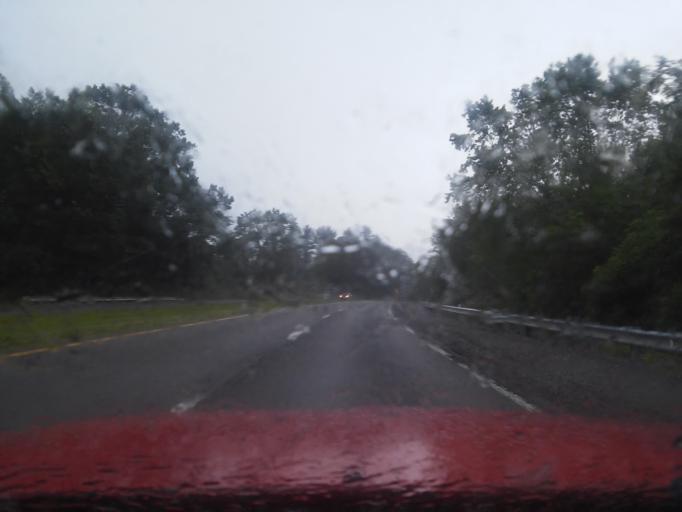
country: US
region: Virginia
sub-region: Montgomery County
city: Prices Fork
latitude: 37.2983
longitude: -80.5030
